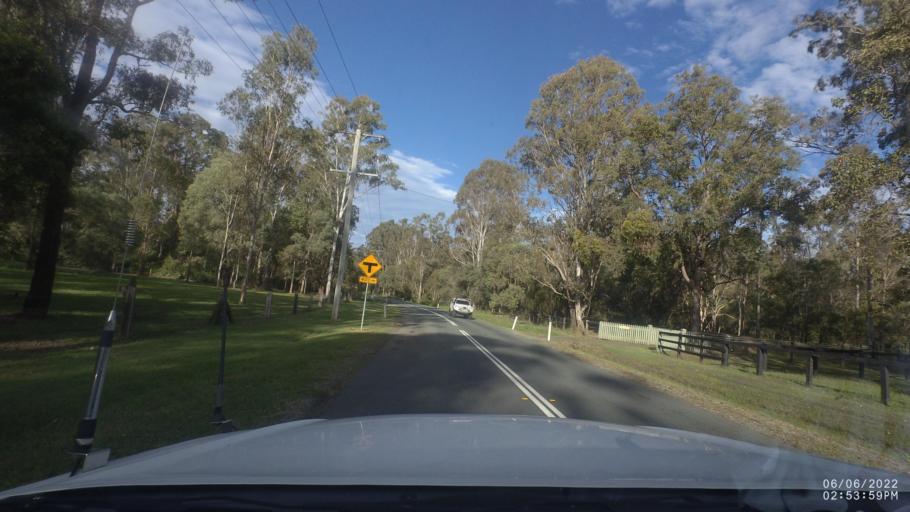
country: AU
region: Queensland
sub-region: Logan
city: Cedar Vale
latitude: -27.8547
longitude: 153.0448
